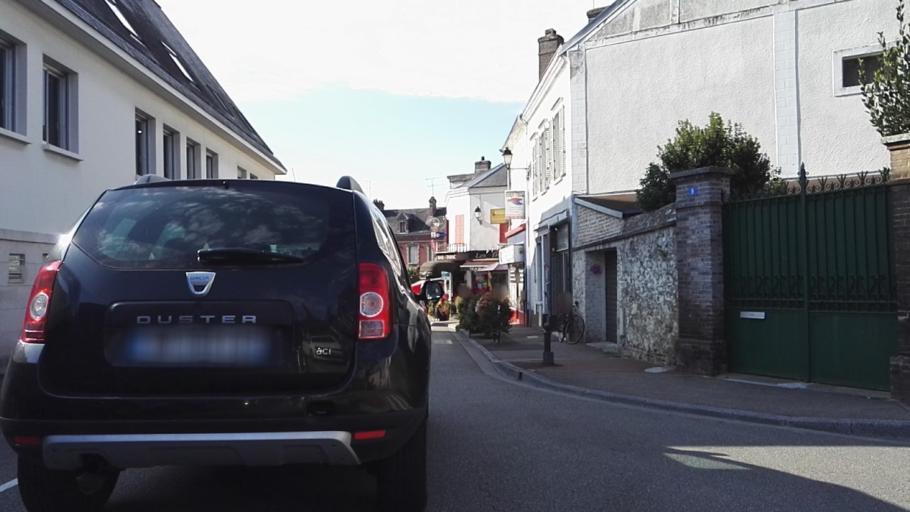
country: FR
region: Haute-Normandie
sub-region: Departement de l'Eure
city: Pacy-sur-Eure
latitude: 49.0148
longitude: 1.3817
